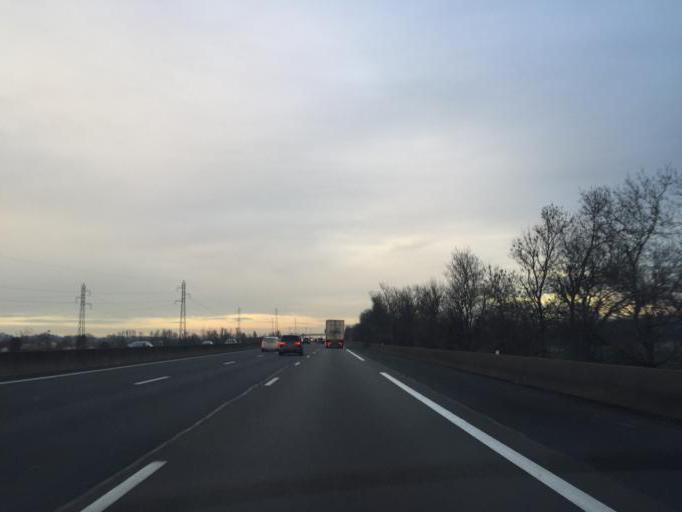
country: FR
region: Bourgogne
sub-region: Departement de Saone-et-Loire
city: La Chapelle-de-Guinchay
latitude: 46.1965
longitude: 4.7776
